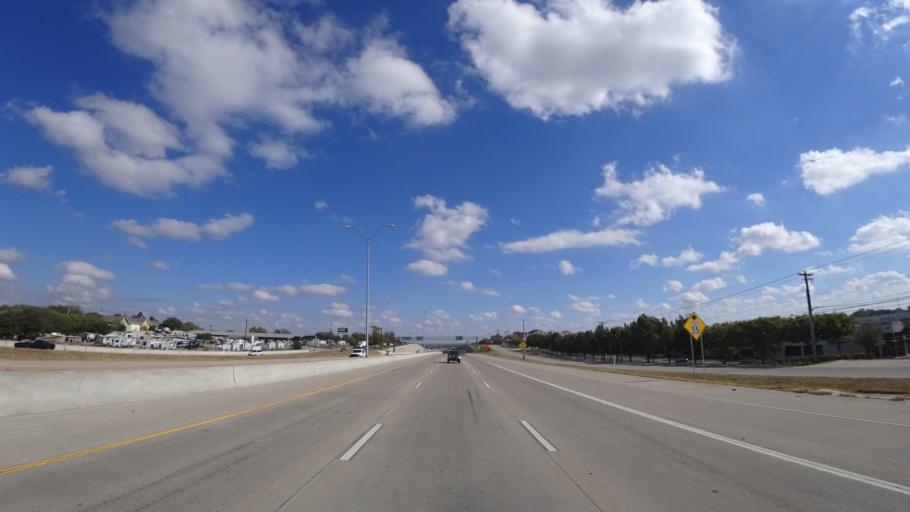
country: US
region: Texas
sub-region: Travis County
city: Austin
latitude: 30.2161
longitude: -97.6975
